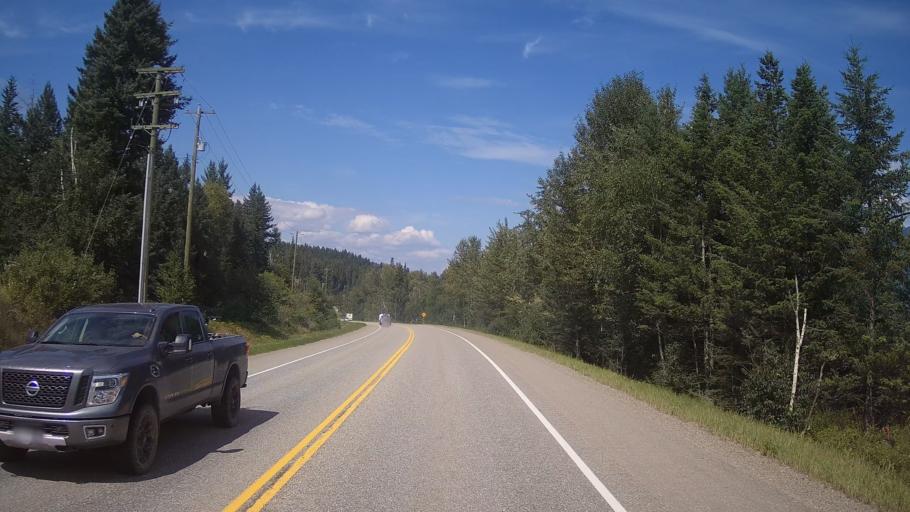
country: CA
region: British Columbia
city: Kamloops
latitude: 51.3138
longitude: -120.1803
